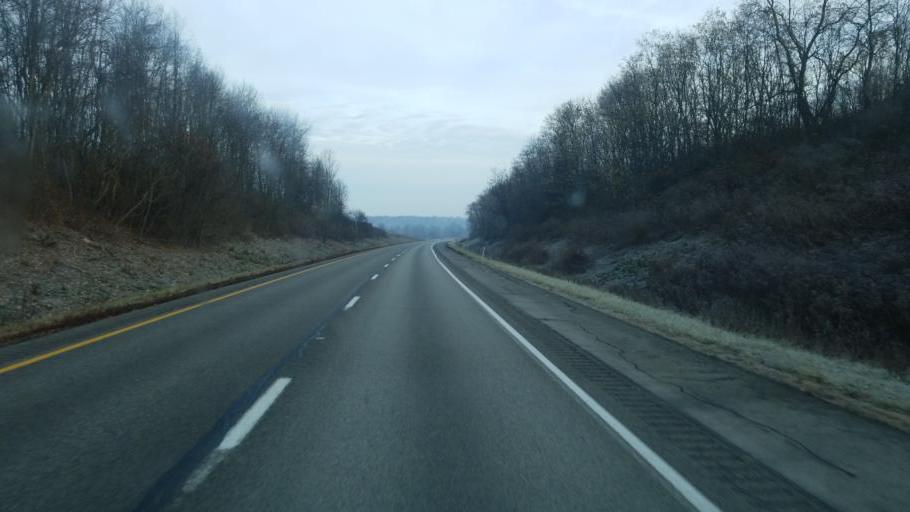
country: US
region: Pennsylvania
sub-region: Mercer County
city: Mercer
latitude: 41.2185
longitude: -80.1640
